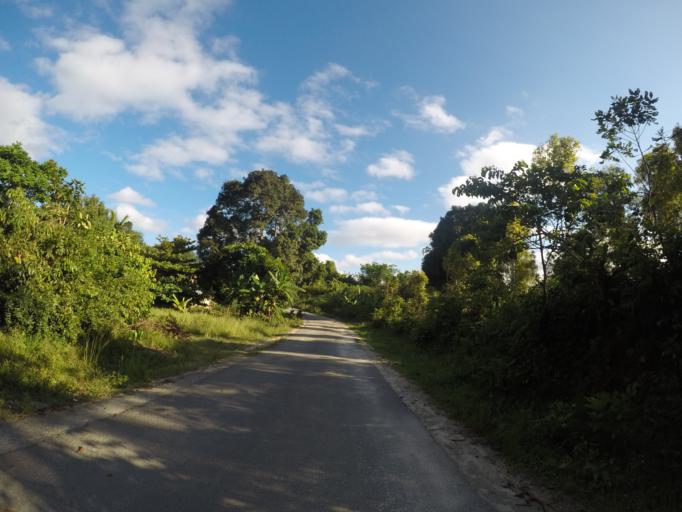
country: TZ
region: Pemba South
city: Mtambile
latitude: -5.3568
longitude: 39.7089
